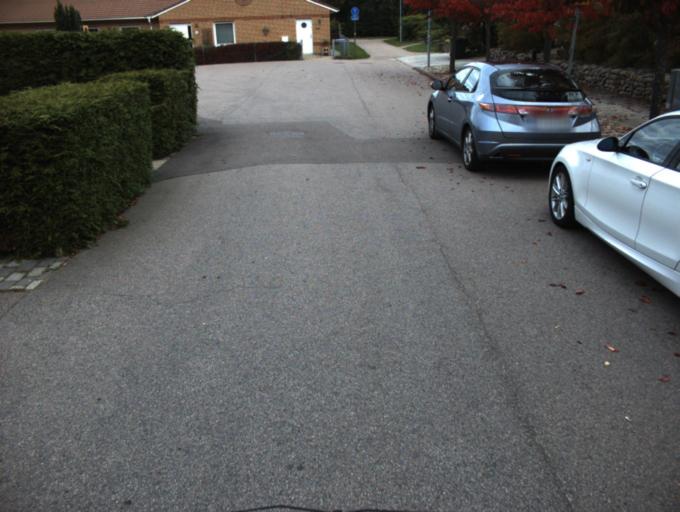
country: SE
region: Skane
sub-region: Helsingborg
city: Helsingborg
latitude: 56.0398
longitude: 12.7504
